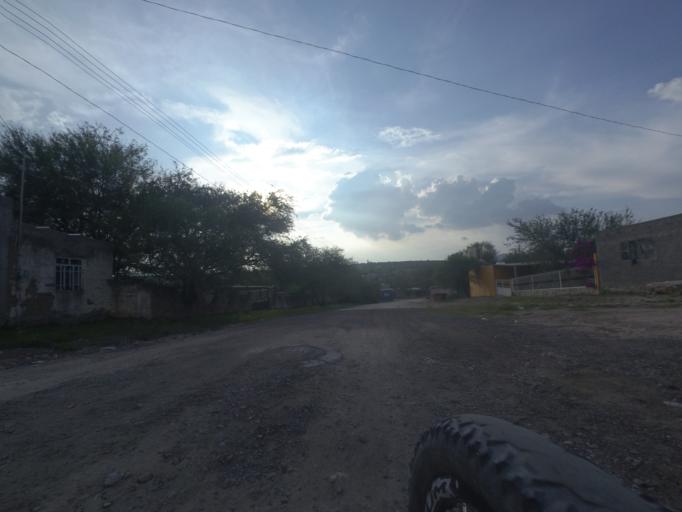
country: MX
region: Aguascalientes
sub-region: Aguascalientes
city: Los Canos
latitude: 21.7765
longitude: -102.3728
